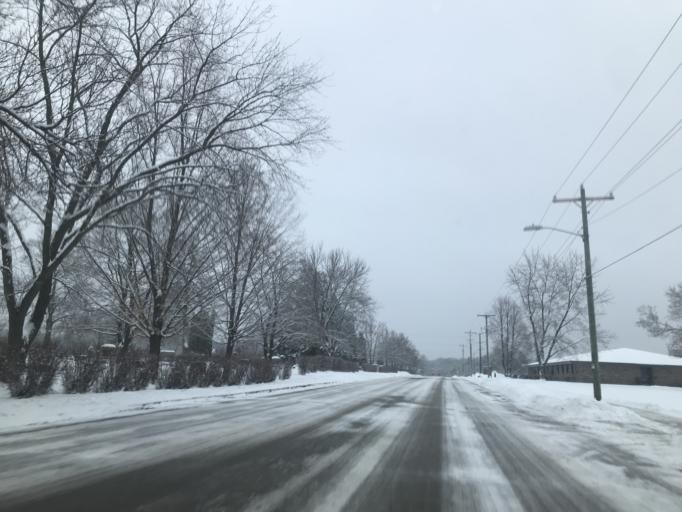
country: US
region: Wisconsin
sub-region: Oconto County
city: Oconto Falls
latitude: 44.8674
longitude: -88.1297
